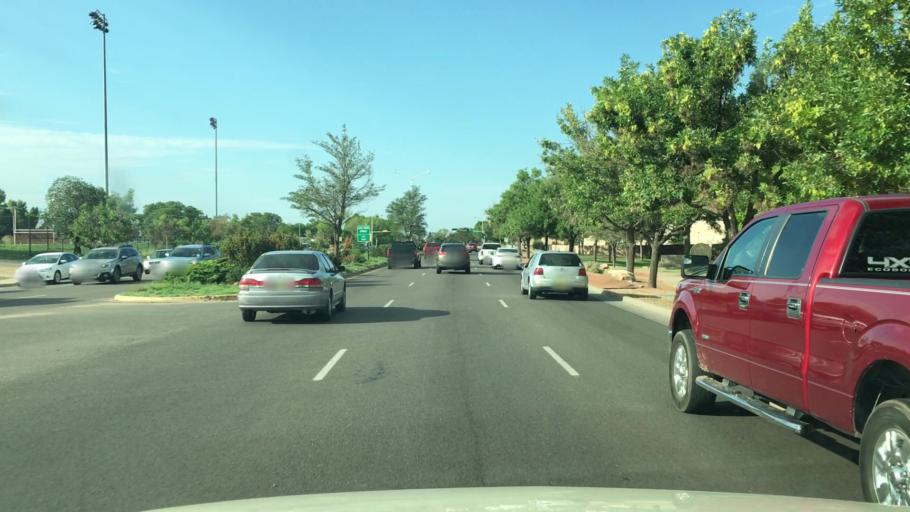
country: US
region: New Mexico
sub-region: Santa Fe County
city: Santa Fe
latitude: 35.6730
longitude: -105.9542
